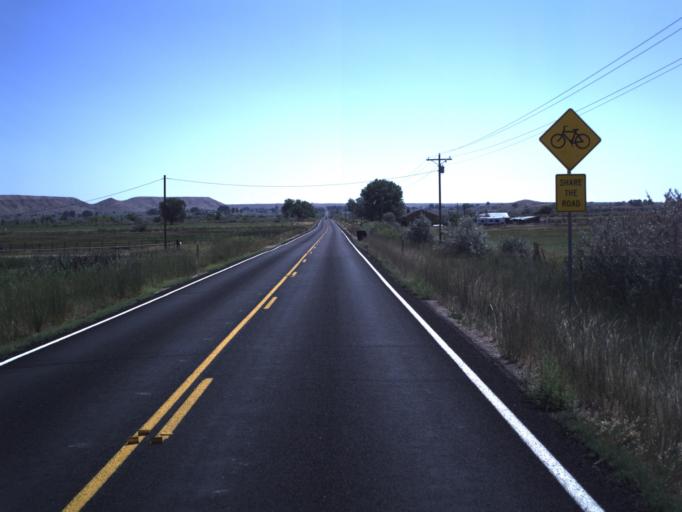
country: US
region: Utah
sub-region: Duchesne County
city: Roosevelt
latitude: 40.4037
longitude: -109.8586
